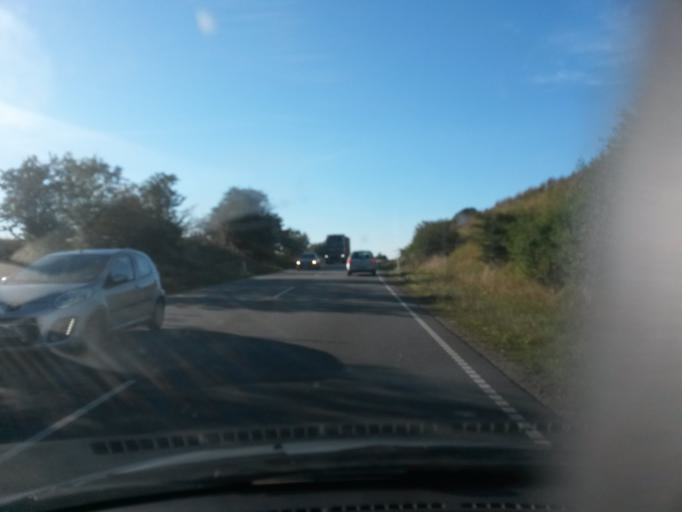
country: DK
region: Central Jutland
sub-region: Favrskov Kommune
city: Hammel
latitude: 56.2461
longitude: 9.7780
